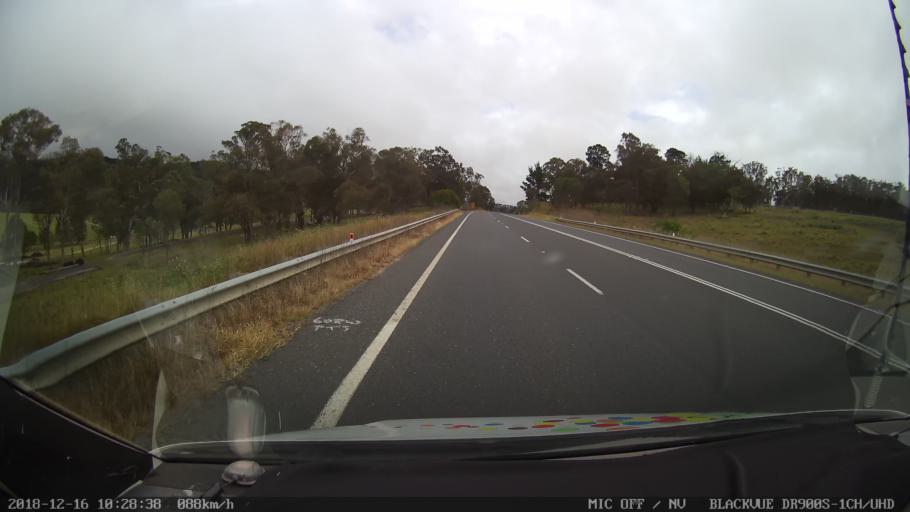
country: AU
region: New South Wales
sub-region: Tenterfield Municipality
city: Carrolls Creek
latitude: -29.1186
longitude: 151.9966
